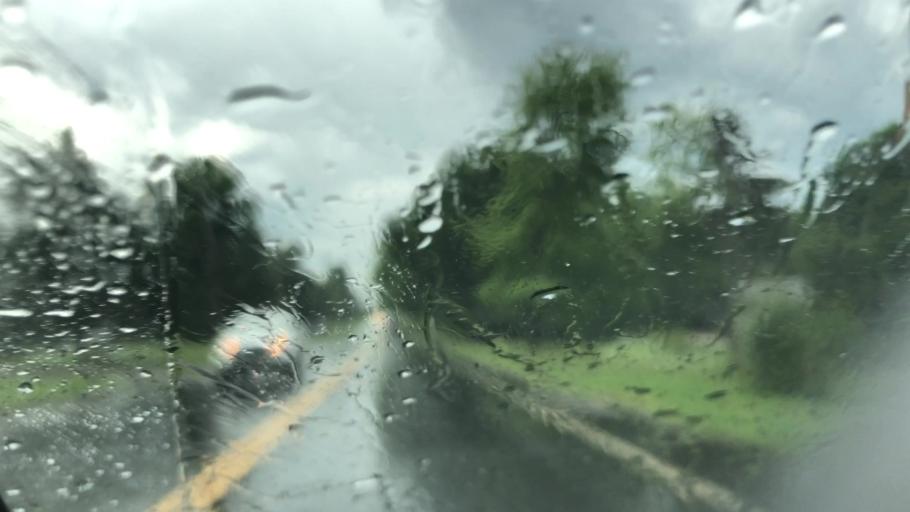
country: US
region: Ohio
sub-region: Stark County
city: Massillon
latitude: 40.8294
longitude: -81.5026
